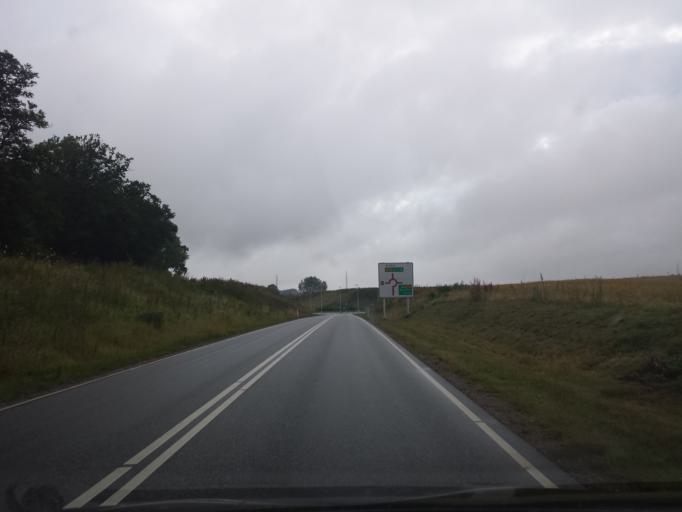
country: DK
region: South Denmark
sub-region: Sonderborg Kommune
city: Grasten
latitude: 54.9494
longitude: 9.6358
